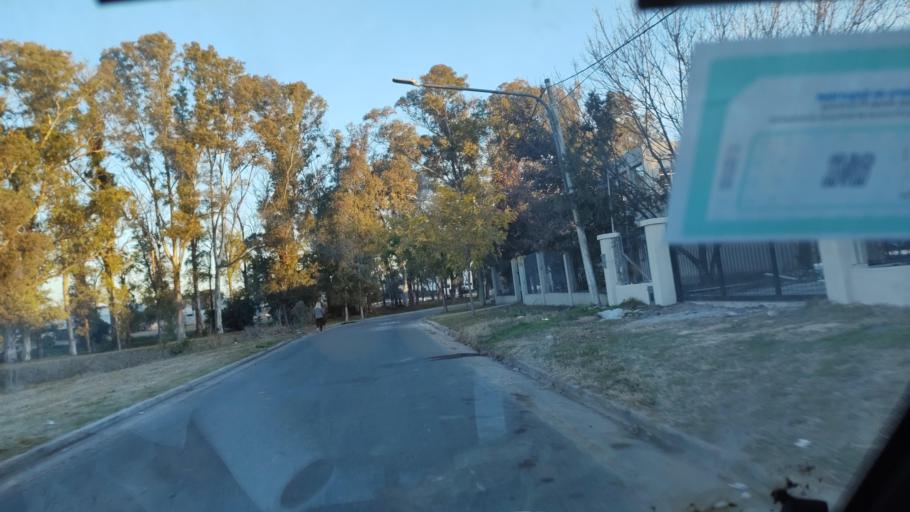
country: AR
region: Buenos Aires
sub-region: Partido de La Plata
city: La Plata
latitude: -34.9022
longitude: -58.0269
